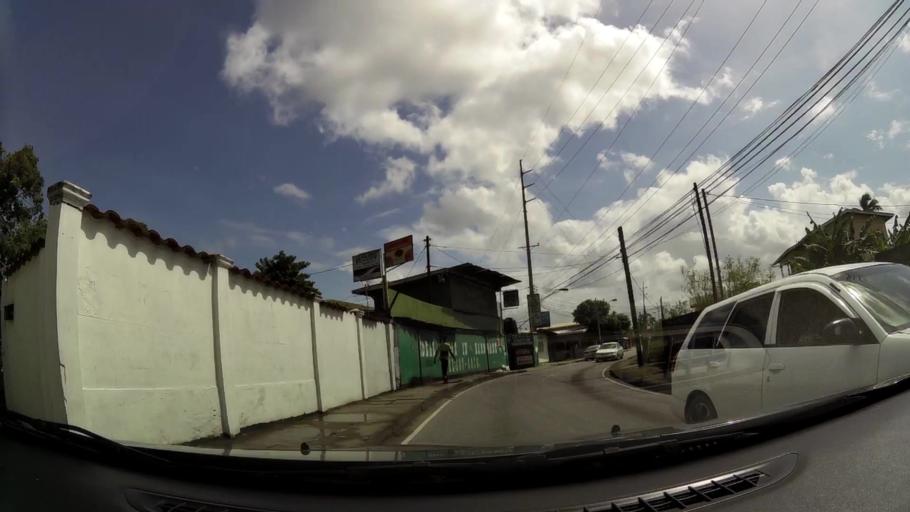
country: TT
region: Borough of Arima
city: Arima
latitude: 10.6378
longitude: -61.2769
